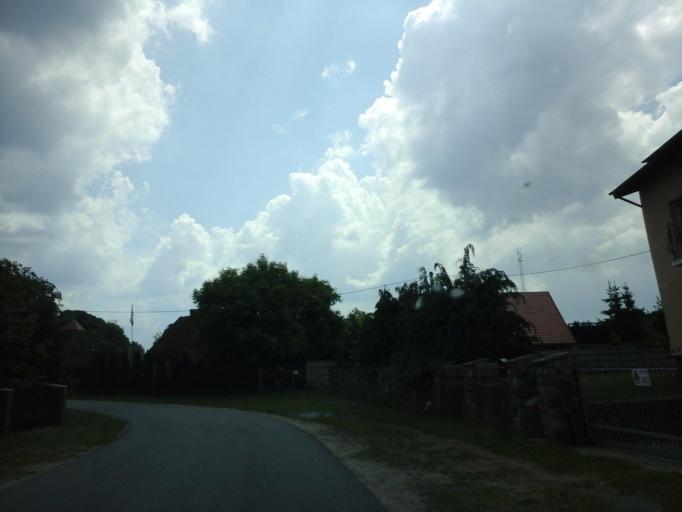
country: PL
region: West Pomeranian Voivodeship
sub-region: Powiat choszczenski
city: Drawno
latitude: 53.2069
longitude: 15.8387
